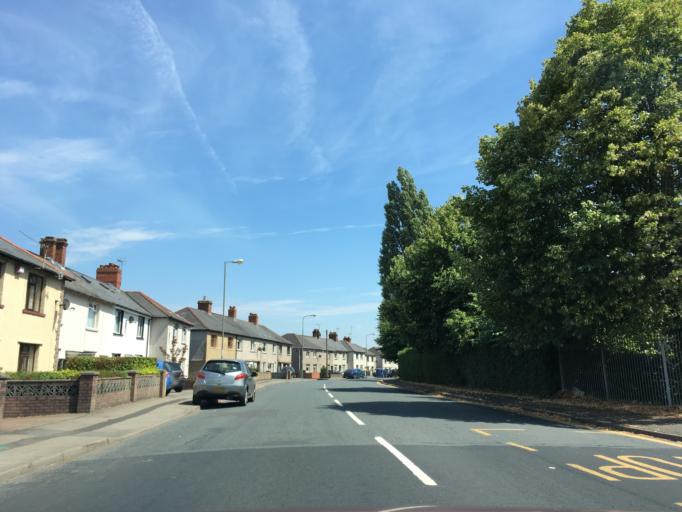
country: GB
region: Wales
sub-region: Caerphilly County Borough
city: Risca
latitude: 51.6021
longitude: -3.0886
